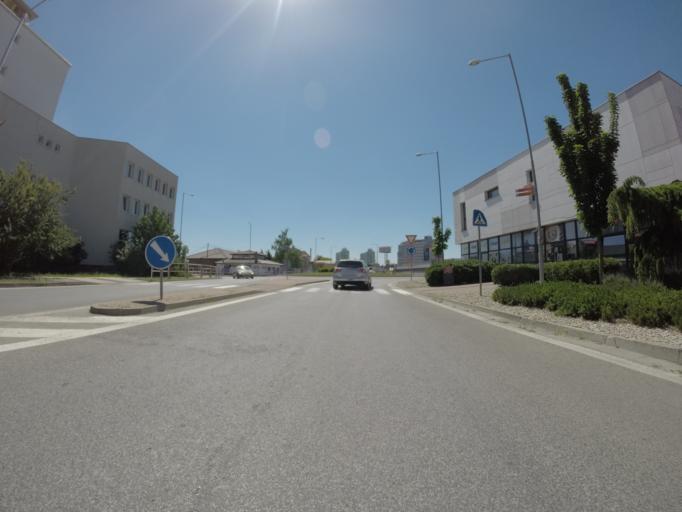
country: SK
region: Trnavsky
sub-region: Okres Galanta
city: Galanta
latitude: 48.1879
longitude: 17.7268
